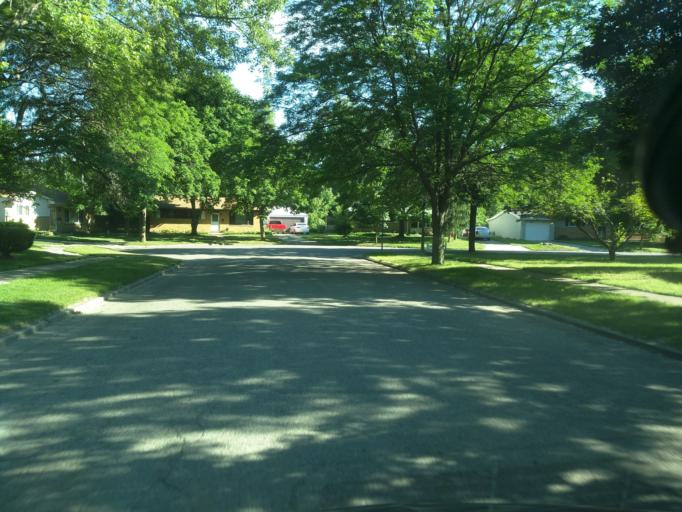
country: US
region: Michigan
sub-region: Ingham County
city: Lansing
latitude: 42.6880
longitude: -84.5928
